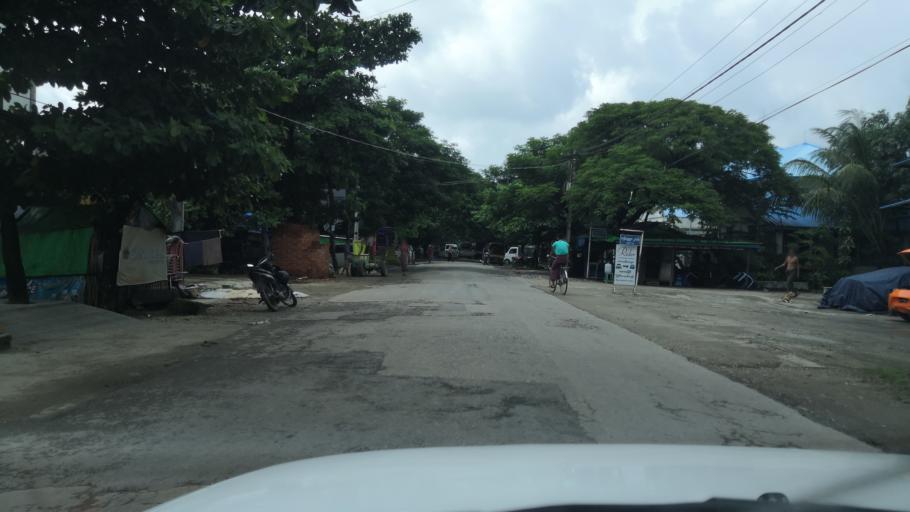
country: MM
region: Yangon
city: Yangon
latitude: 16.8861
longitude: 96.1767
